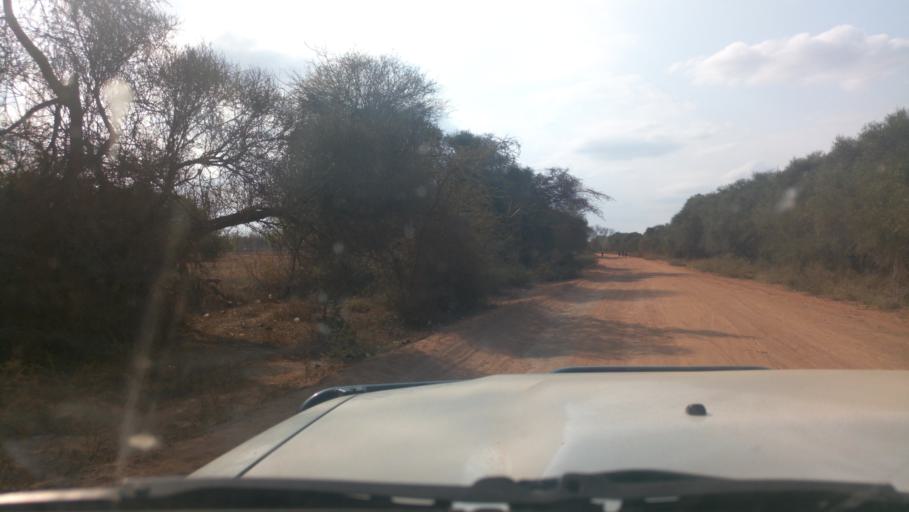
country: KE
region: Makueni
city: Wote
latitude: -1.6694
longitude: 37.9196
